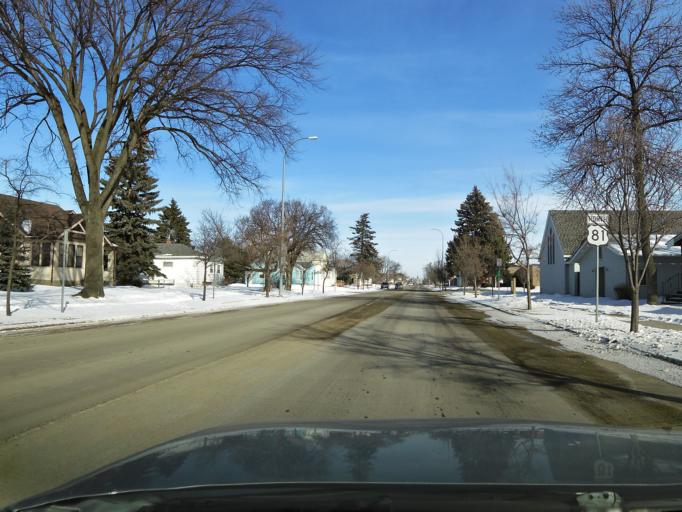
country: US
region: North Dakota
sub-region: Walsh County
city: Grafton
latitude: 48.4128
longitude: -97.4112
